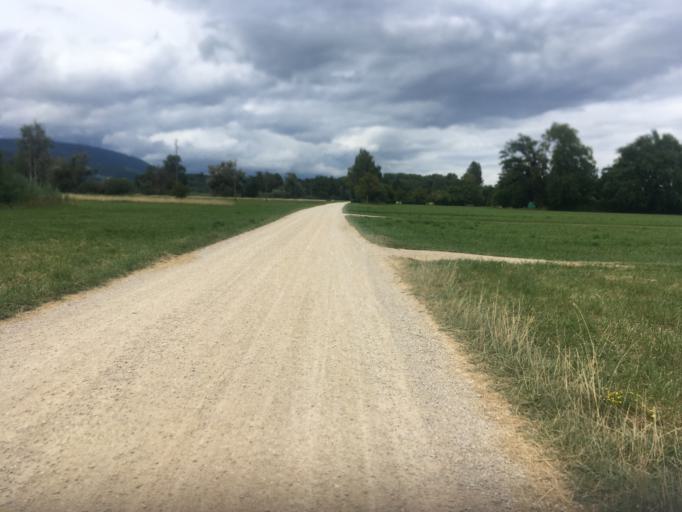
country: CH
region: Bern
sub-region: Jura bernois
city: La Neuveville
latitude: 47.0568
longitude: 7.1237
